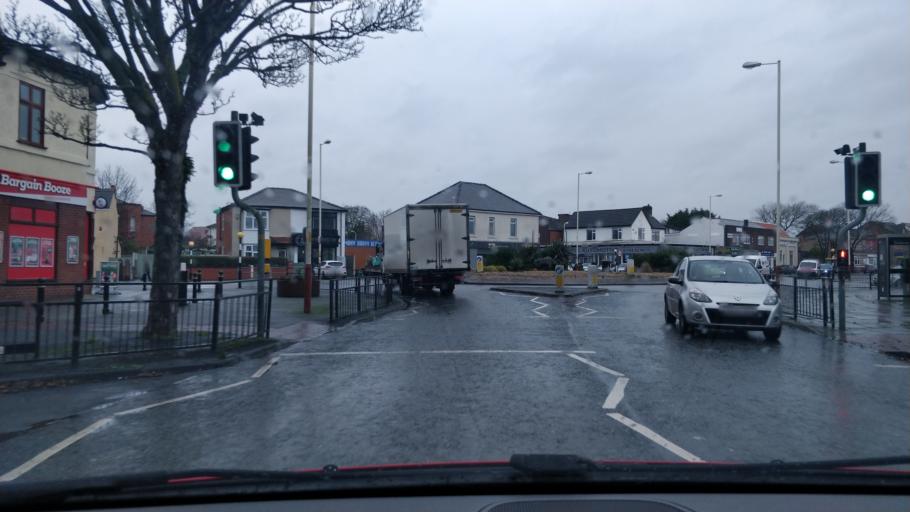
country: GB
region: England
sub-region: Sefton
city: Southport
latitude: 53.6026
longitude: -3.0336
